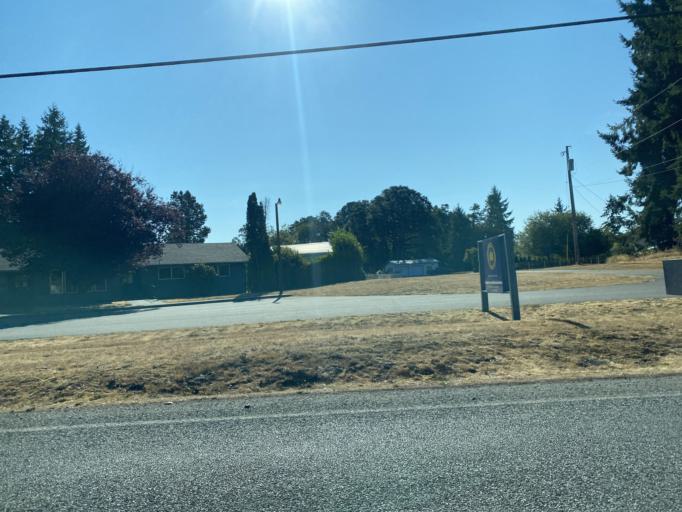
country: US
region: Washington
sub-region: Thurston County
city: Tanglewilde-Thompson Place
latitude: 46.9870
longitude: -122.7398
